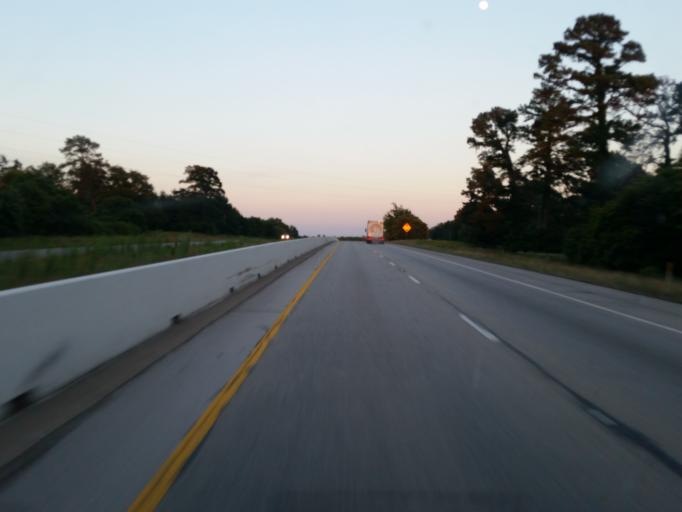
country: US
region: Texas
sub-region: Smith County
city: Hideaway
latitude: 32.4738
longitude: -95.4719
